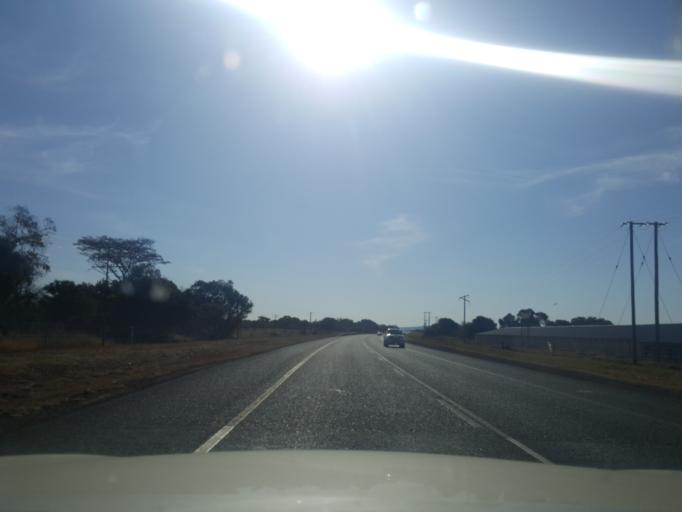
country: ZA
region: North-West
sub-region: Ngaka Modiri Molema District Municipality
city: Zeerust
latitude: -25.5530
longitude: 26.2109
